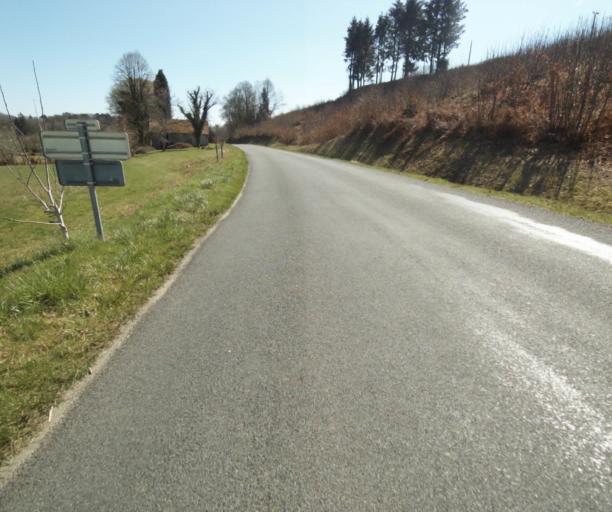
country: FR
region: Limousin
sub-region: Departement de la Correze
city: Saint-Mexant
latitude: 45.2786
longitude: 1.6612
